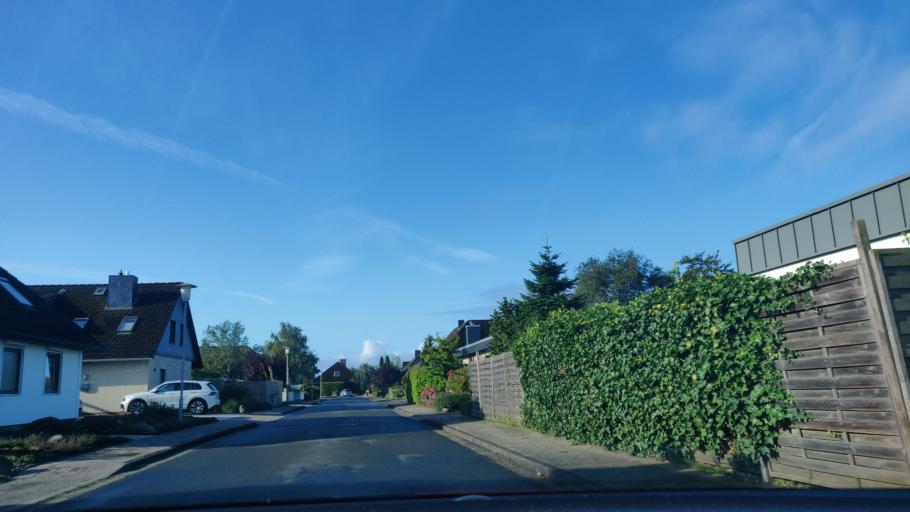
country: DE
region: Lower Saxony
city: Cuxhaven
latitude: 53.8779
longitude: 8.6785
